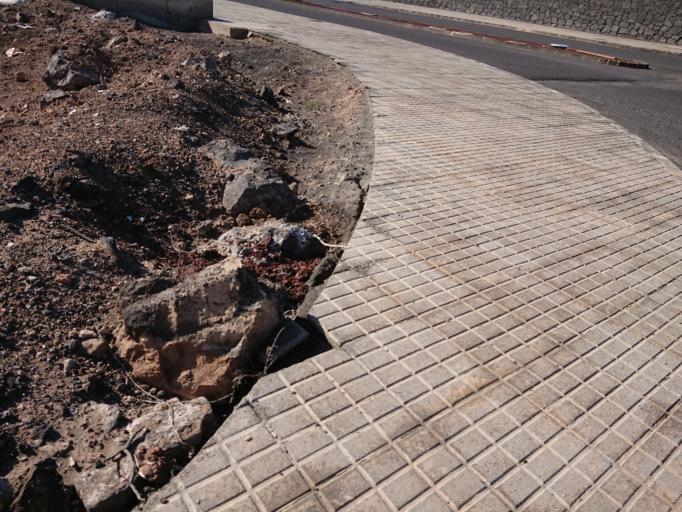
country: ES
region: Canary Islands
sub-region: Provincia de Las Palmas
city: Playa Blanca
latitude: 28.8719
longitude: -13.8636
